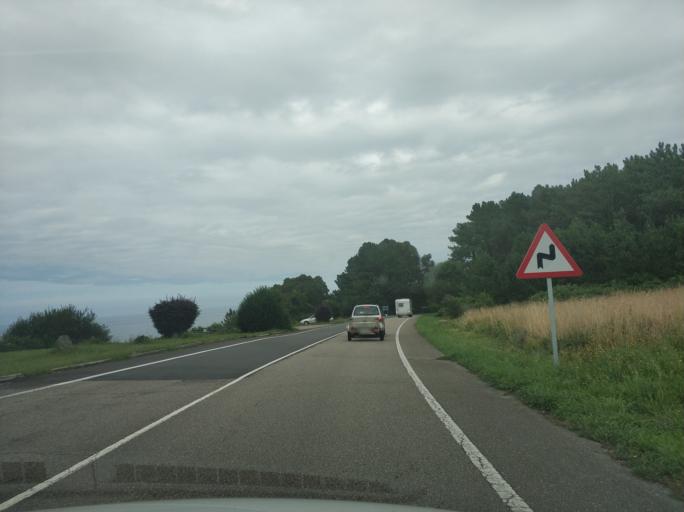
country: ES
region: Asturias
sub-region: Province of Asturias
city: Cudillero
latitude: 43.5653
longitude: -6.1568
